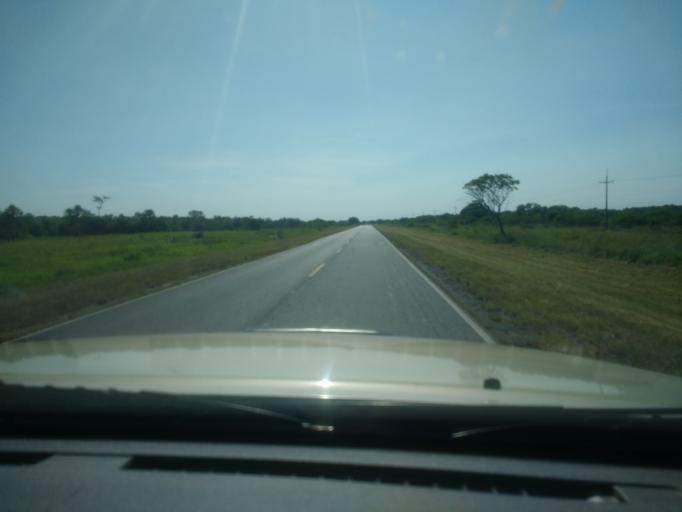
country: PY
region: Presidente Hayes
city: Benjamin Aceval
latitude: -24.9215
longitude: -57.5855
